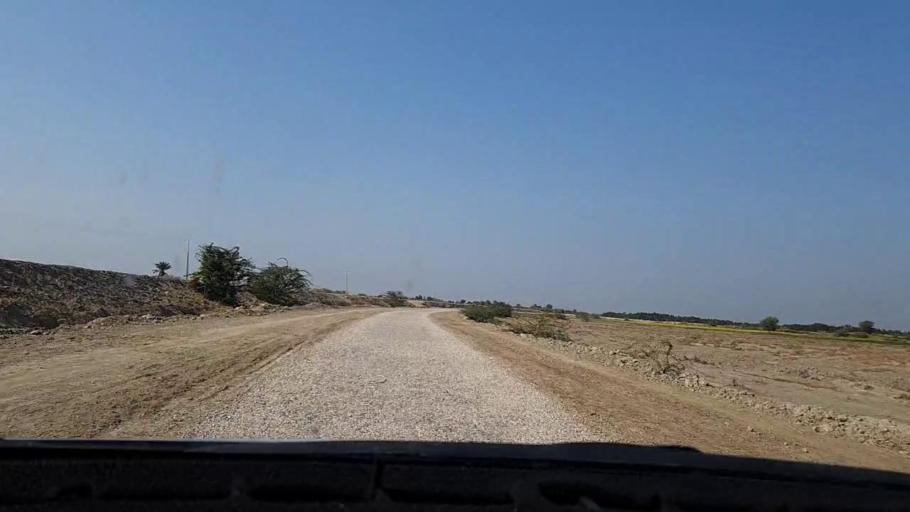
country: PK
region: Sindh
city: Tando Mittha Khan
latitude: 25.8206
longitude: 69.2942
